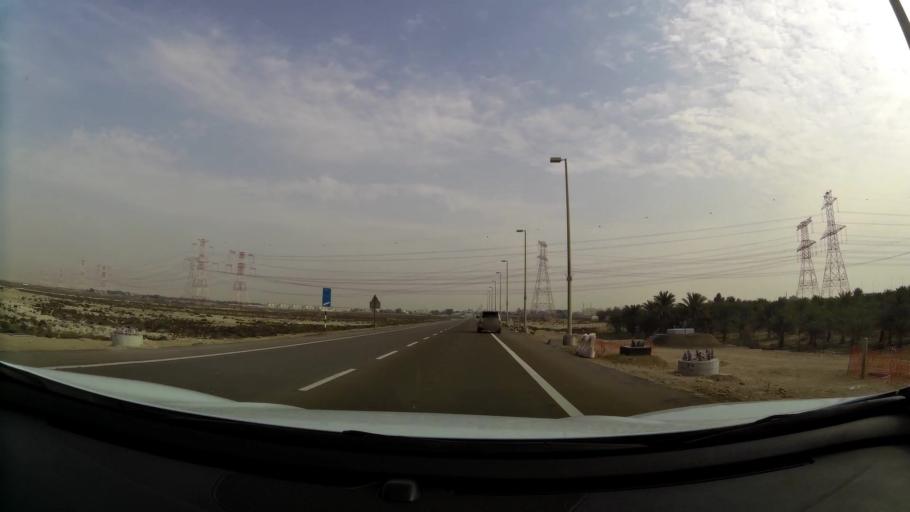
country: AE
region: Abu Dhabi
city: Abu Dhabi
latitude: 24.6611
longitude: 54.7450
